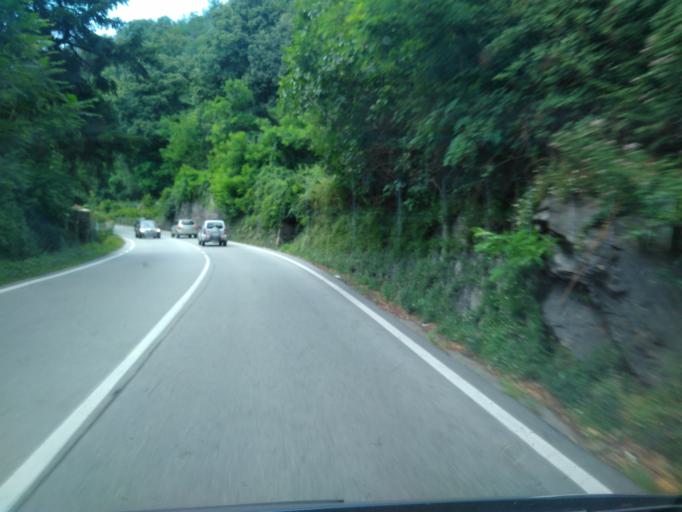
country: IT
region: Piedmont
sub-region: Provincia Verbano-Cusio-Ossola
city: Santino
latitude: 45.9388
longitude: 8.5154
